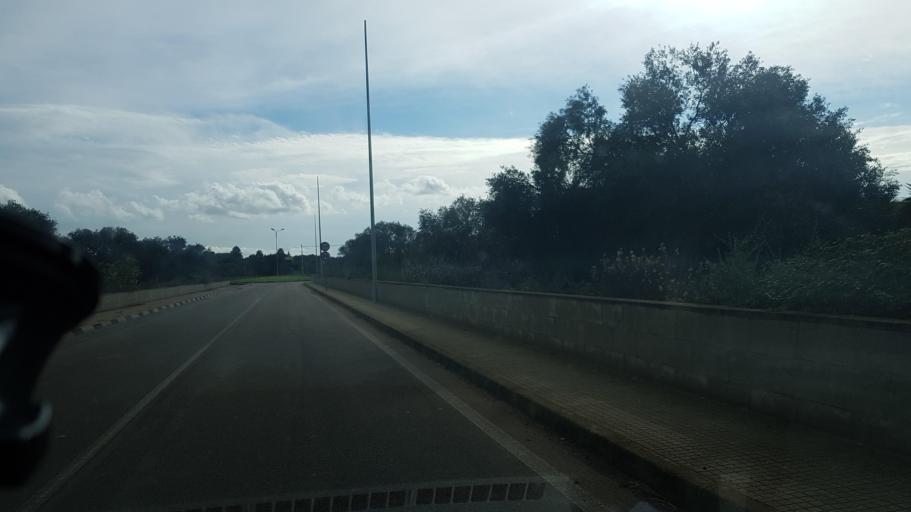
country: IT
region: Apulia
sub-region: Provincia di Brindisi
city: San Vito dei Normanni
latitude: 40.6620
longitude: 17.7153
